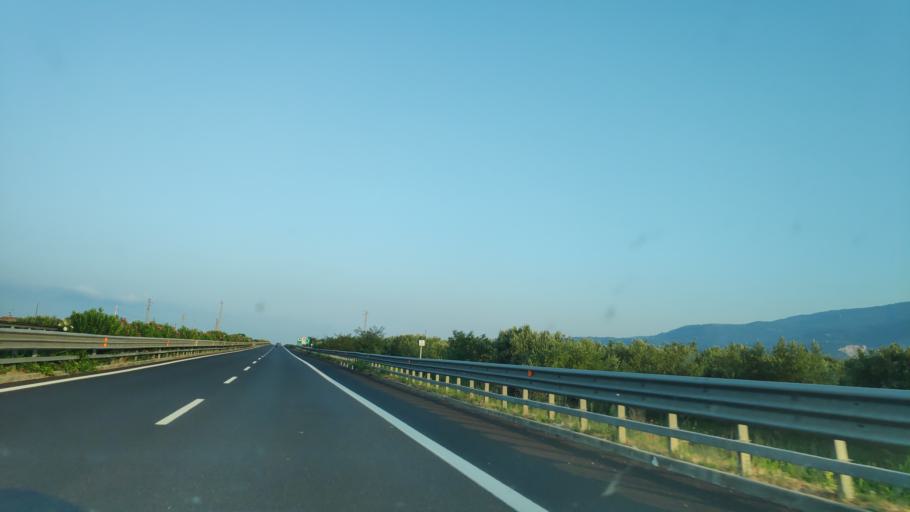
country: IT
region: Calabria
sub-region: Provincia di Catanzaro
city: Santa Eufemia Lamezia
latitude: 38.9241
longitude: 16.2572
